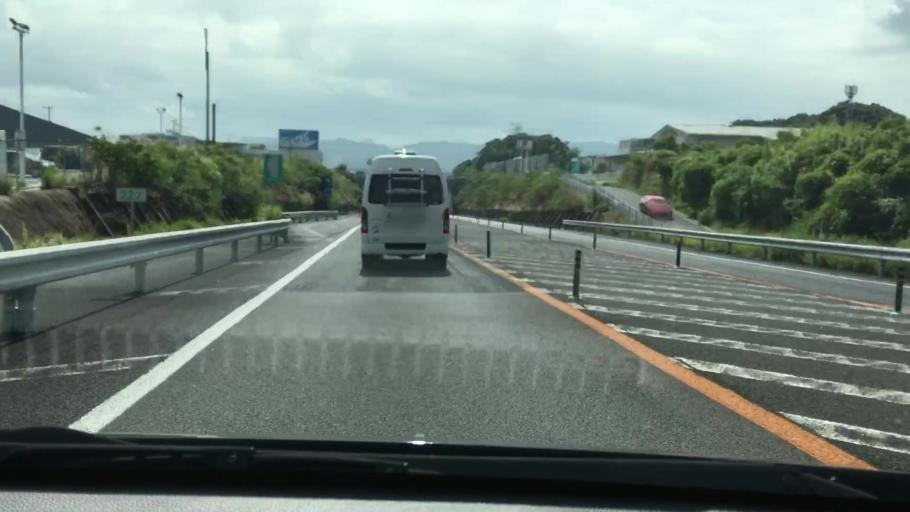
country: JP
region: Nagasaki
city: Sasebo
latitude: 33.1497
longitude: 129.7687
